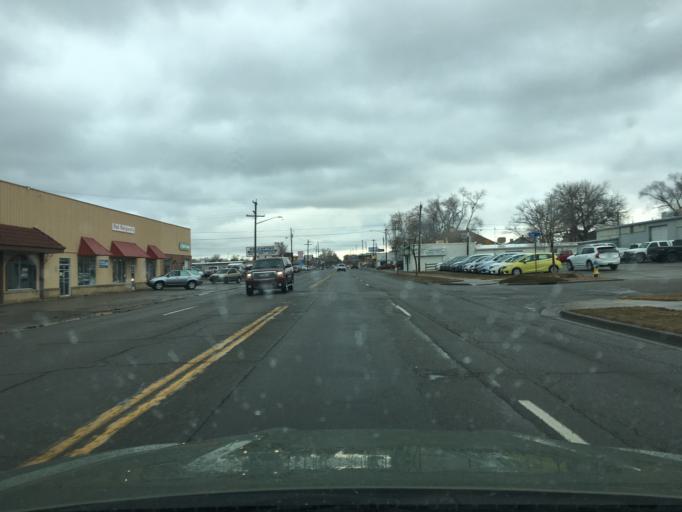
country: US
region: Colorado
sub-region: Mesa County
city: Grand Junction
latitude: 39.0743
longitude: -108.5708
